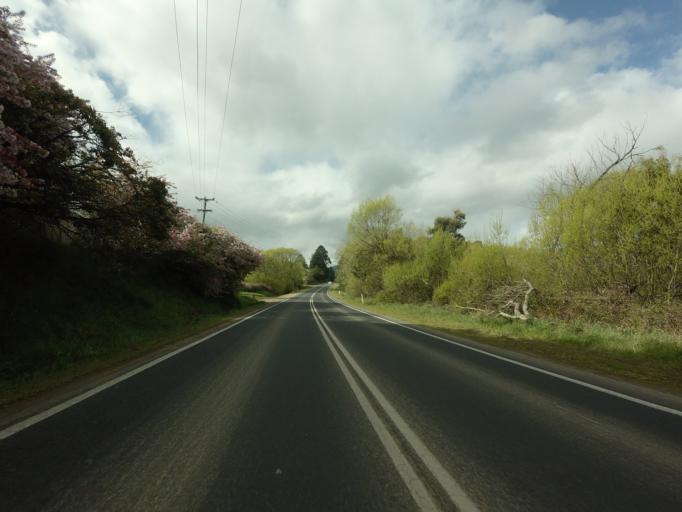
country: AU
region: Tasmania
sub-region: Huon Valley
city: Franklin
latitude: -43.0721
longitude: 147.0190
